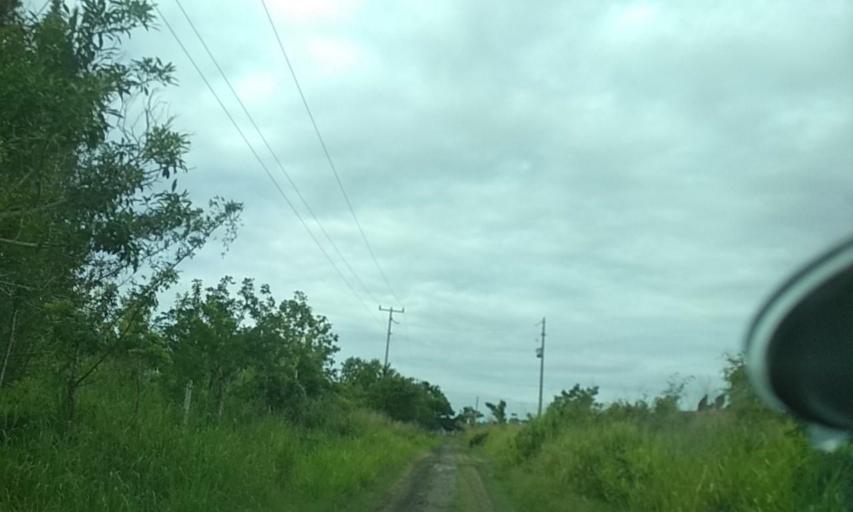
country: MX
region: Veracruz
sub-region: Cazones de Herrera
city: Rancho Nuevo
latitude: 20.6027
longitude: -97.1447
